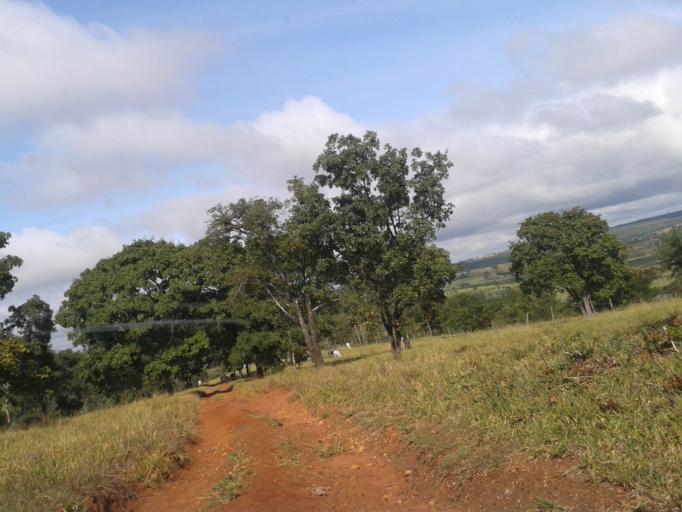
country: BR
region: Minas Gerais
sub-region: Campina Verde
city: Campina Verde
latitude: -19.4249
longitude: -49.6562
